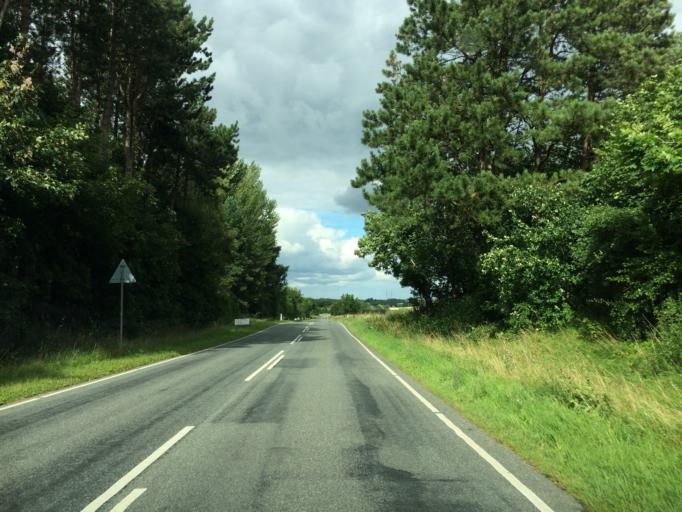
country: DK
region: South Denmark
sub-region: Assens Kommune
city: Harby
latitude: 55.2211
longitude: 10.1698
